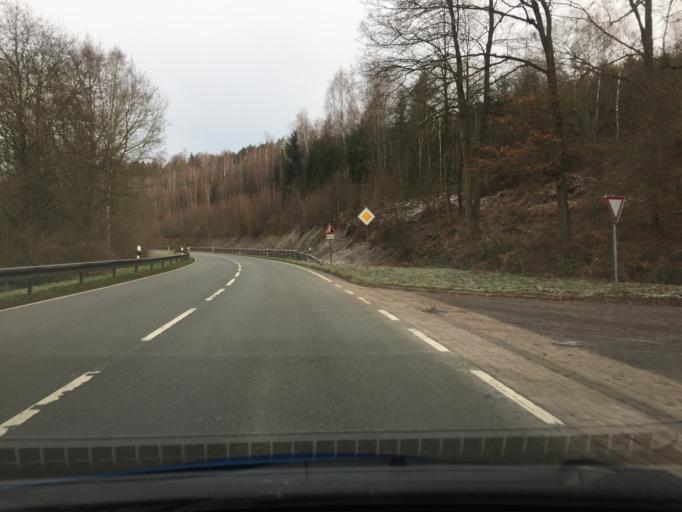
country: DE
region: Lower Saxony
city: Bevern
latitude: 51.8049
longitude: 9.4966
